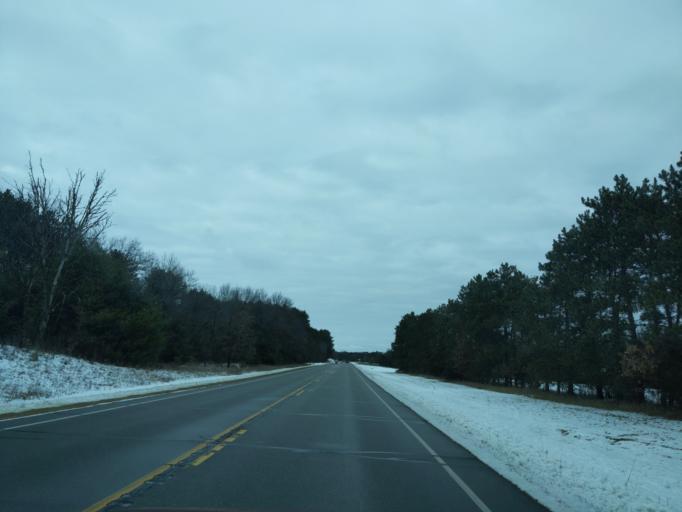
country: US
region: Wisconsin
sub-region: Waushara County
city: Wautoma
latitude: 43.9471
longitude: -89.3176
